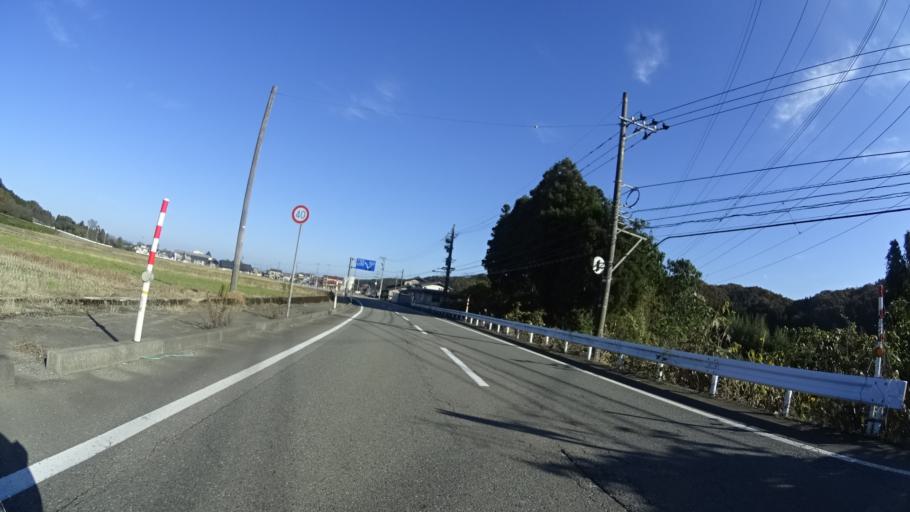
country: JP
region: Ishikawa
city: Komatsu
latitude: 36.2811
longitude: 136.3910
